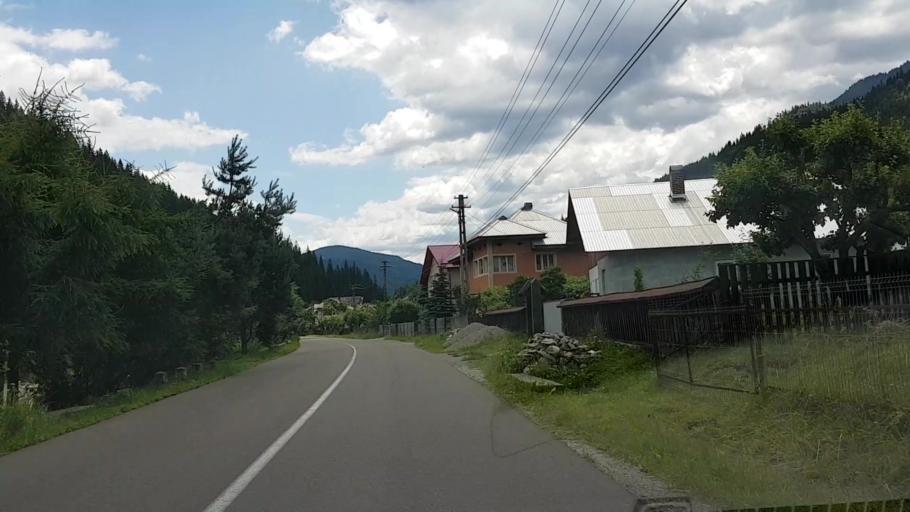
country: RO
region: Suceava
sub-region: Comuna Crucea
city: Crucea
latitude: 47.3447
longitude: 25.6083
